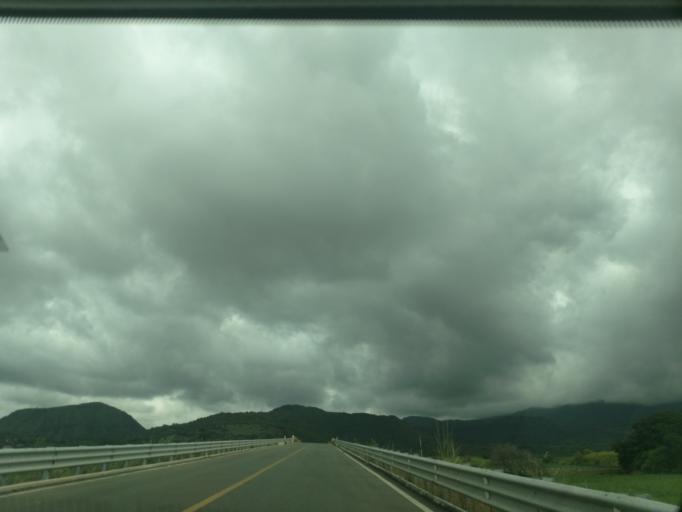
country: MX
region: Nayarit
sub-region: Tepic
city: La Corregidora
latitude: 21.4546
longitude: -104.8053
